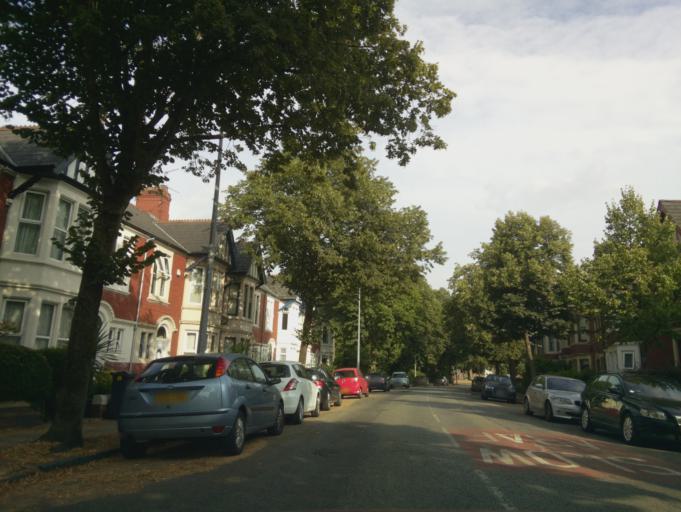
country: GB
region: Wales
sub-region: Cardiff
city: Cardiff
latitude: 51.4935
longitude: -3.1573
